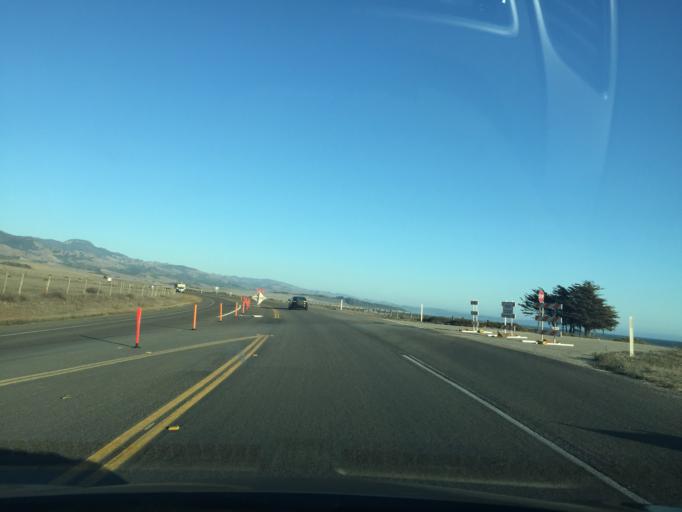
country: US
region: California
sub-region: San Luis Obispo County
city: Cambria
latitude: 35.6539
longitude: -121.2426
